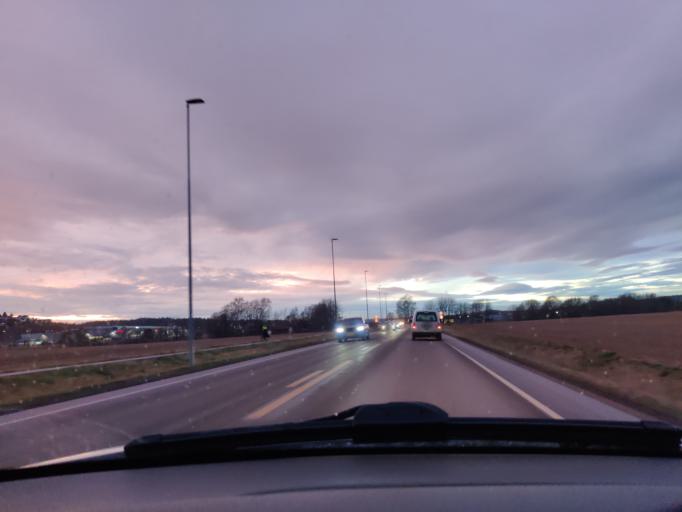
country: NO
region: Vestfold
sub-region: Tonsberg
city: Tonsberg
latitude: 59.2820
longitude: 10.3753
